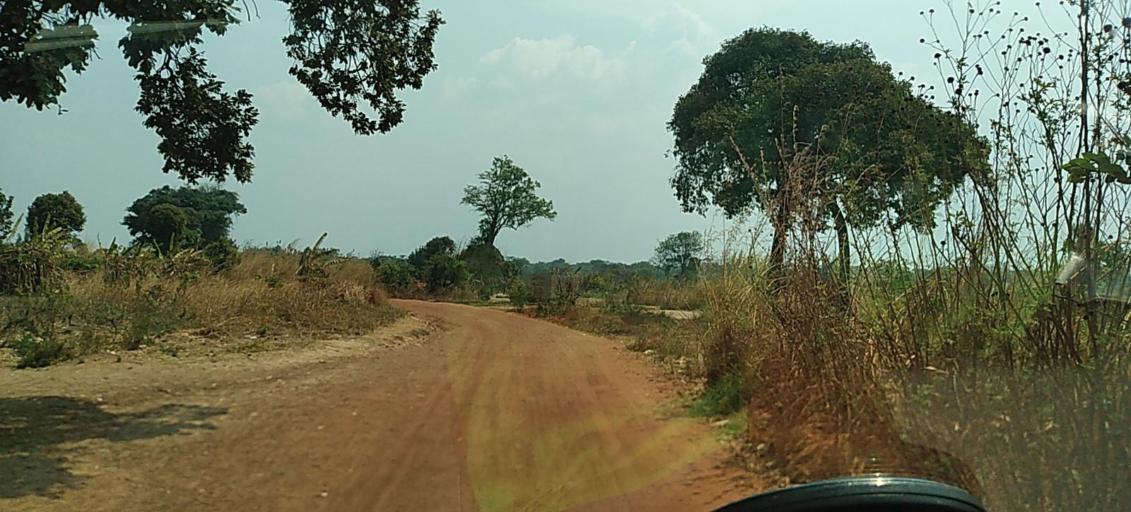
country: ZM
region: North-Western
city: Kansanshi
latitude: -12.0945
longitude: 26.3637
